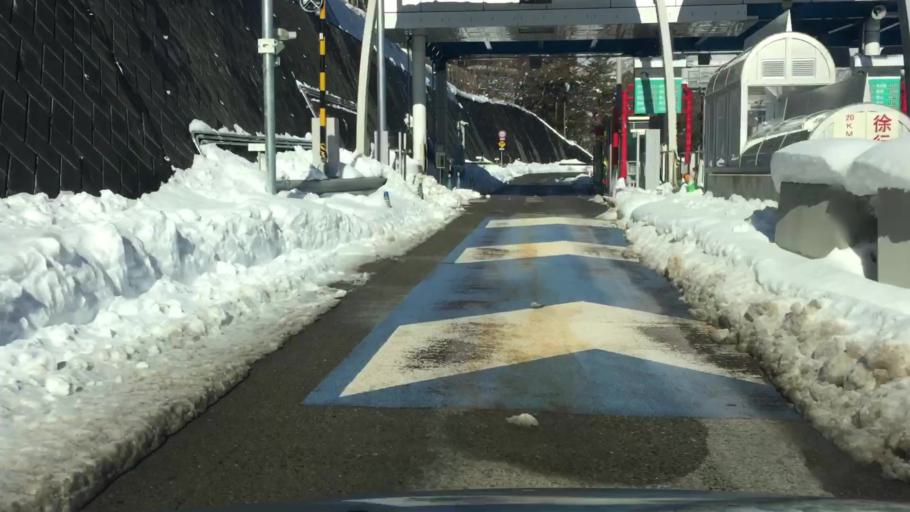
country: JP
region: Gunma
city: Numata
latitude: 36.7475
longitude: 138.9737
